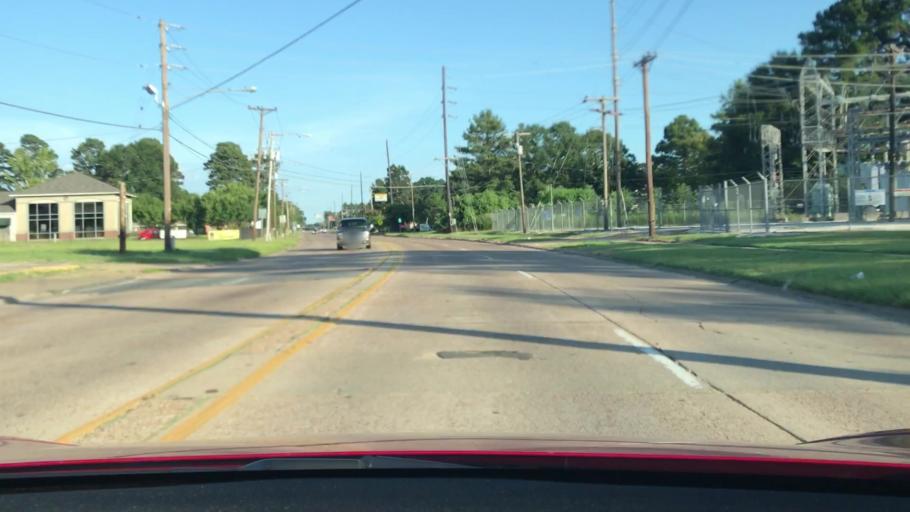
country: US
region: Louisiana
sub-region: Bossier Parish
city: Bossier City
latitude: 32.4312
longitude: -93.7455
